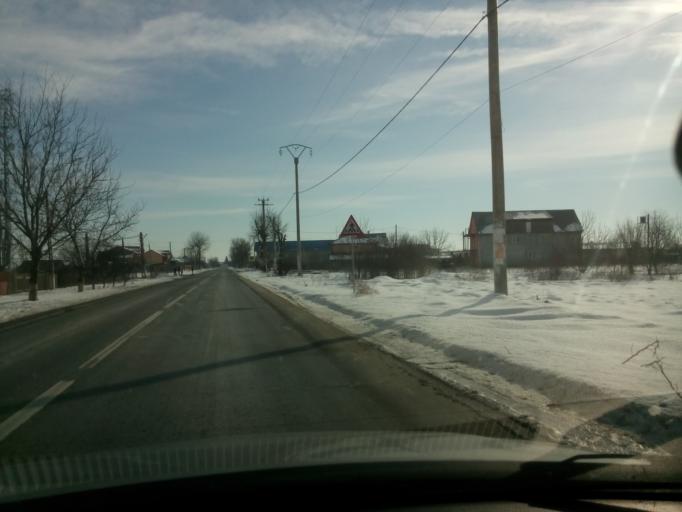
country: RO
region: Calarasi
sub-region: Comuna Frumusani
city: Frumusani
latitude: 44.3062
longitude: 26.2975
